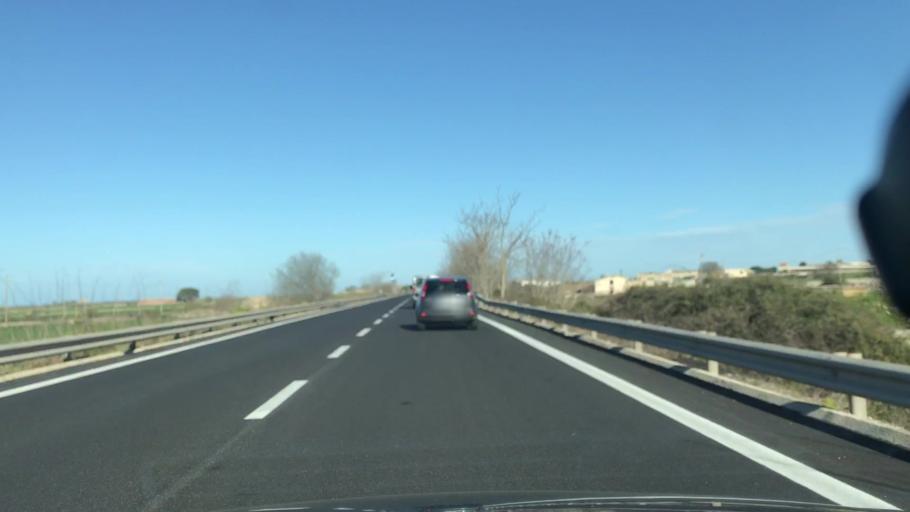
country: IT
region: Sicily
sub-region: Ragusa
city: Ragusa
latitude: 36.9270
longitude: 14.6635
